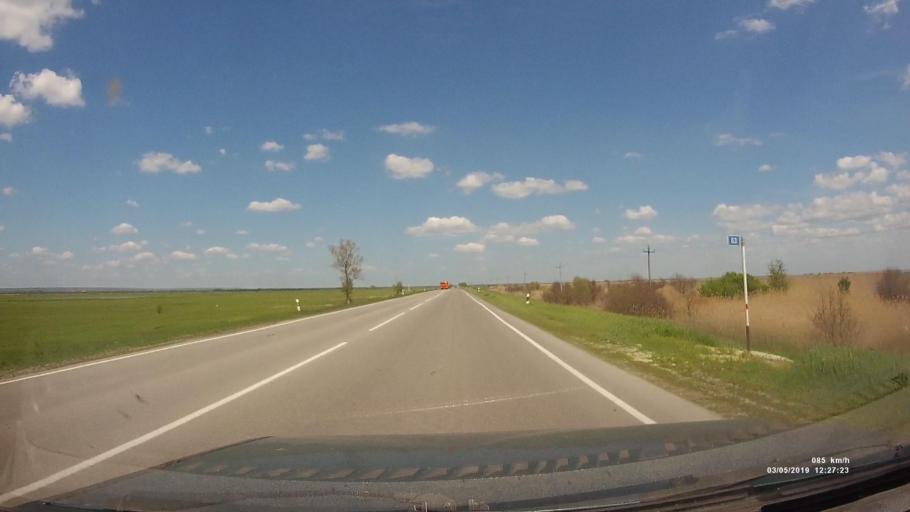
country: RU
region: Rostov
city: Semikarakorsk
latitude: 47.4589
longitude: 40.7207
